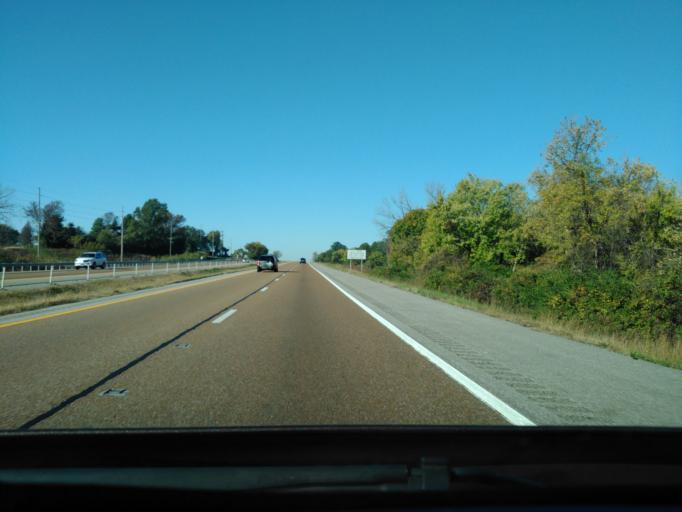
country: US
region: Illinois
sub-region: Madison County
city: Maryville
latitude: 38.7108
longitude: -89.9416
